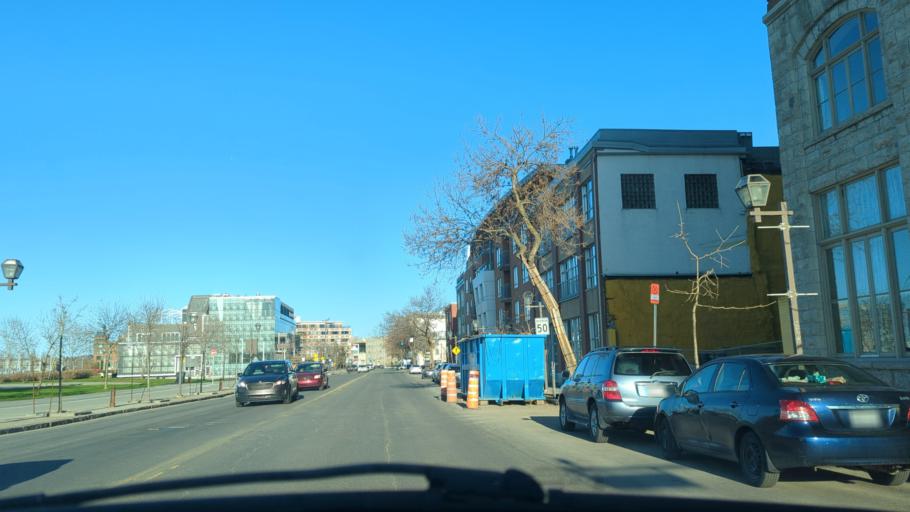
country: CA
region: Quebec
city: Quebec
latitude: 46.8173
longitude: -71.2081
